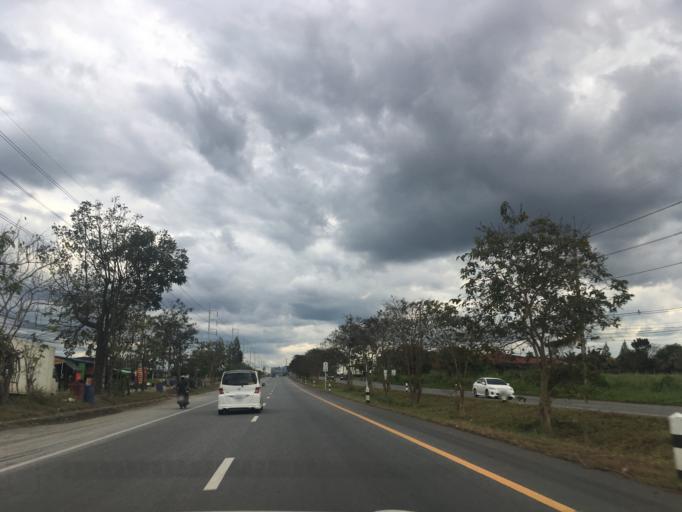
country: TH
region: Chon Buri
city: Nong Yai
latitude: 13.2192
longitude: 101.2369
